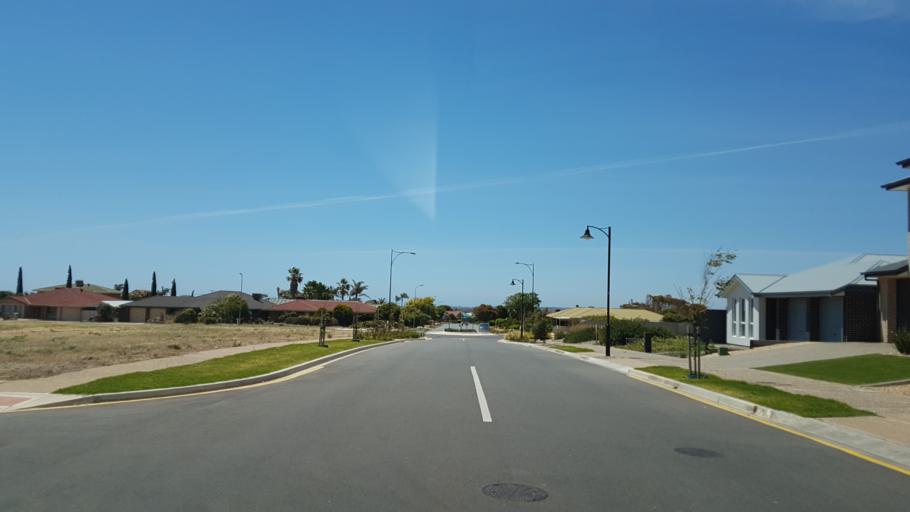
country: AU
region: South Australia
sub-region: Onkaparinga
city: Moana
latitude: -35.2171
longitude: 138.4751
